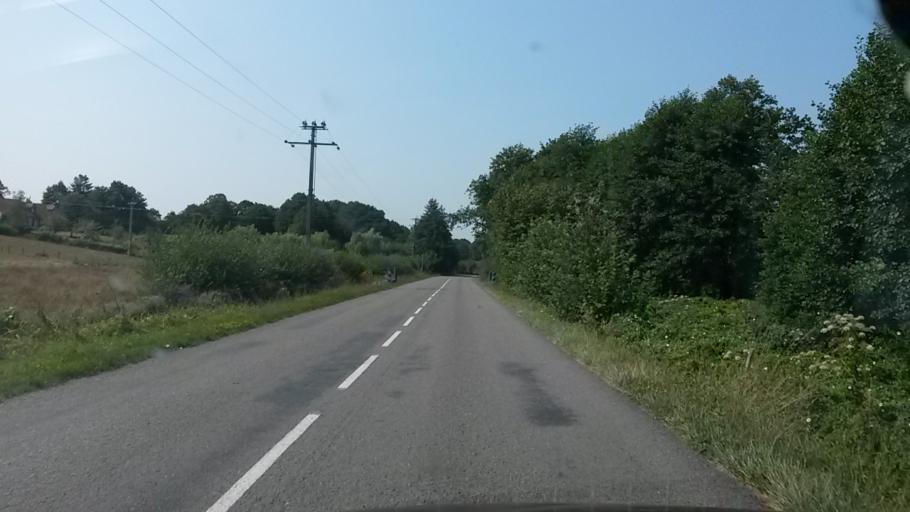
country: FR
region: Pays de la Loire
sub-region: Departement de la Mayenne
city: Saint-Pierre-des-Nids
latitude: 48.4044
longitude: -0.0843
